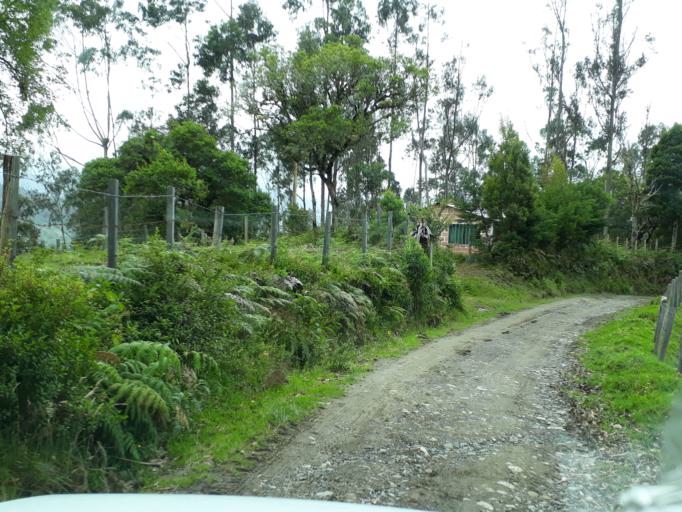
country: CO
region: Cundinamarca
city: Junin
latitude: 4.7536
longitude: -73.6286
